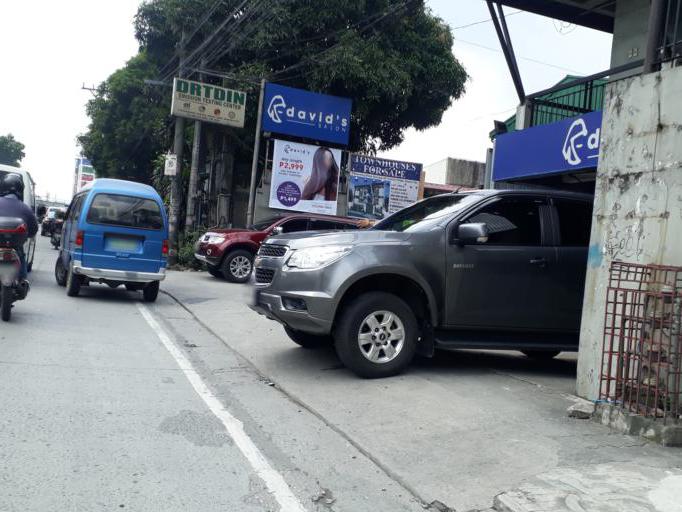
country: PH
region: Calabarzon
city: Bagong Pagasa
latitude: 14.6736
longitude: 121.0321
